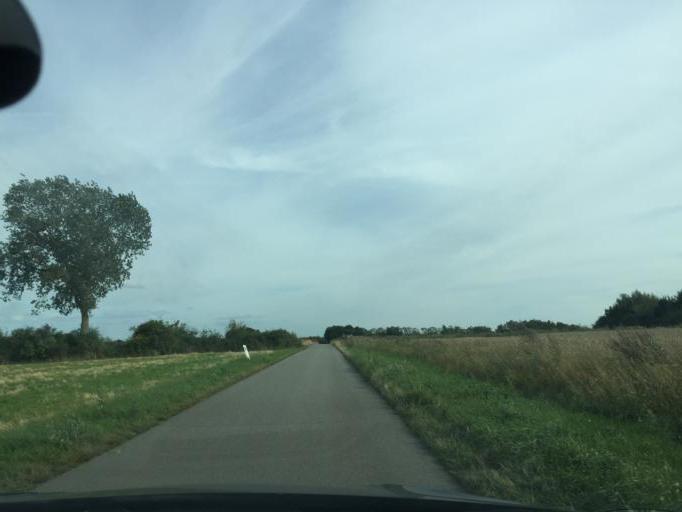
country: DK
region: South Denmark
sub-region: Kerteminde Kommune
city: Langeskov
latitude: 55.3358
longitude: 10.5531
